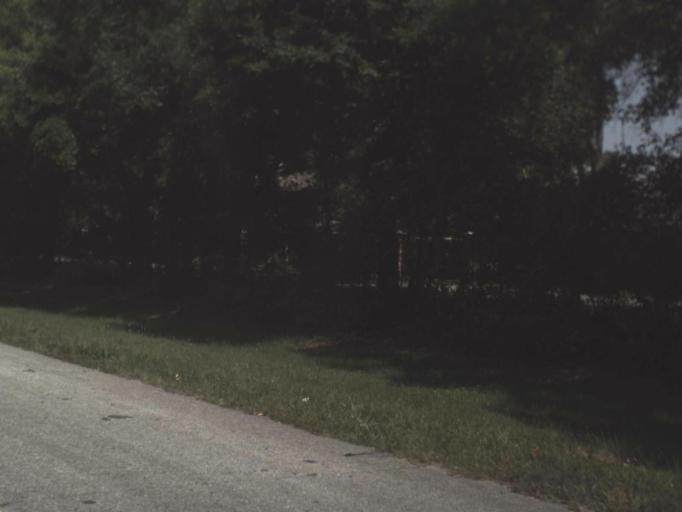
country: US
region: Florida
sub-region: Duval County
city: Jacksonville
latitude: 30.2928
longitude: -81.5906
